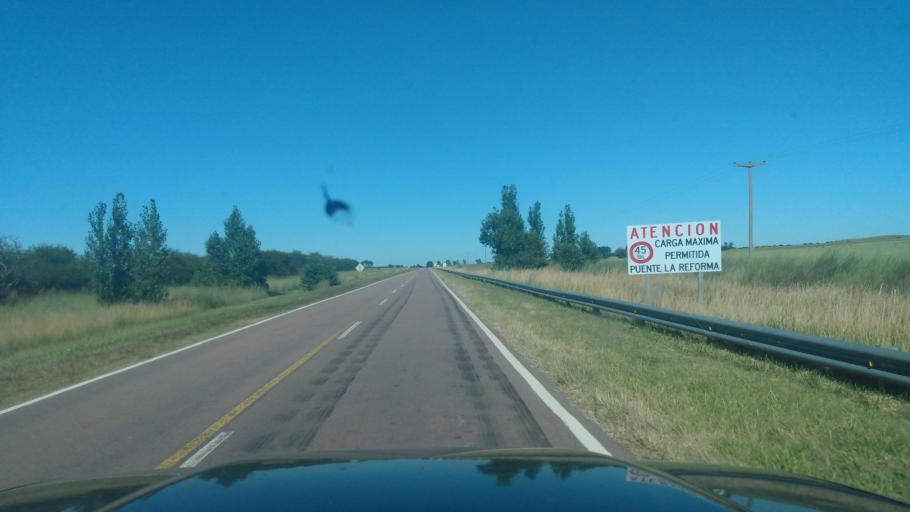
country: AR
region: La Pampa
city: General Acha
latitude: -37.3139
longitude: -64.2968
